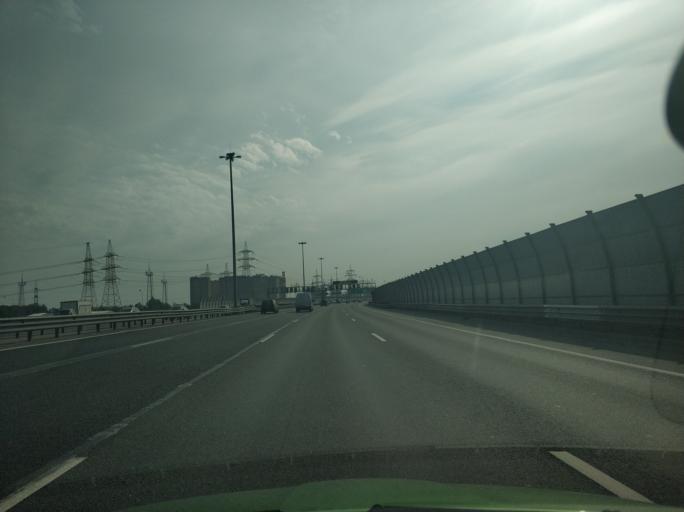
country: RU
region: Leningrad
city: Murino
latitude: 60.0466
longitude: 30.4295
